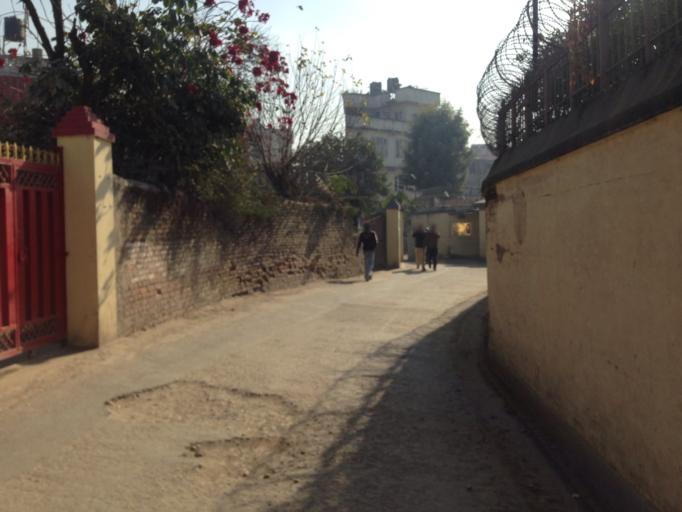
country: NP
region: Central Region
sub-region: Bagmati Zone
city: Kathmandu
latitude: 27.7227
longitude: 85.3221
